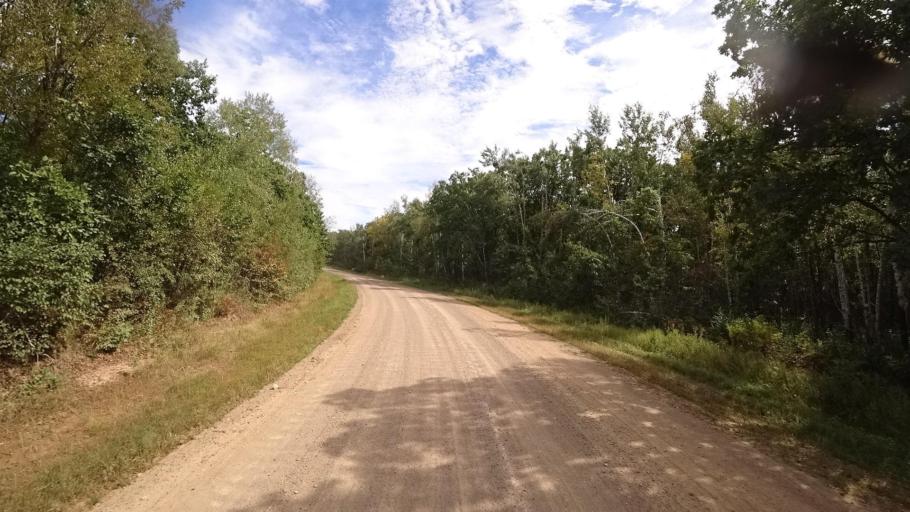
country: RU
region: Primorskiy
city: Yakovlevka
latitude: 44.5491
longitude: 133.5827
